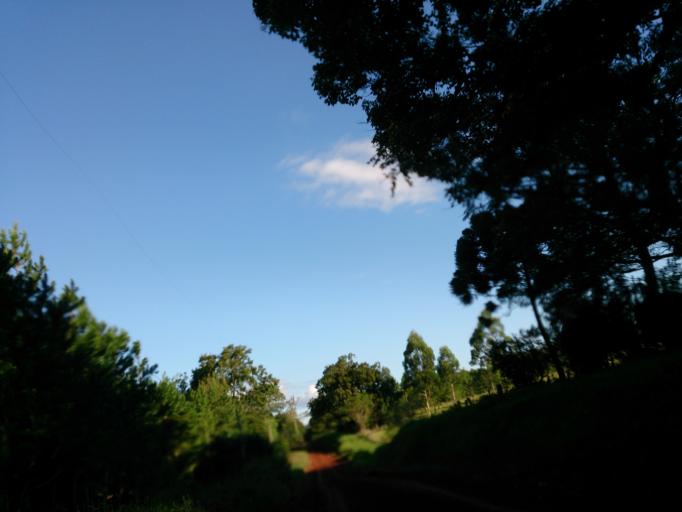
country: AR
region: Misiones
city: Guarani
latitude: -27.5579
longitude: -55.1793
